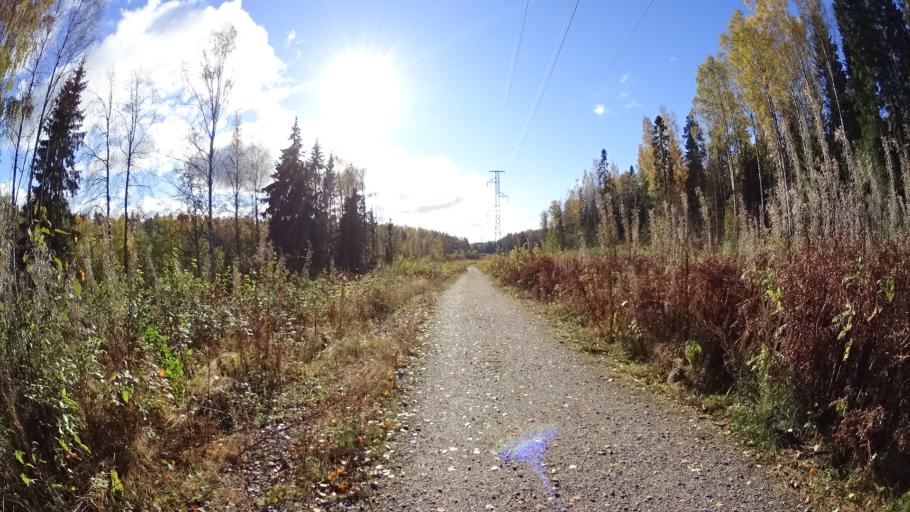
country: FI
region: Uusimaa
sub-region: Helsinki
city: Kilo
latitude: 60.2506
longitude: 24.7990
